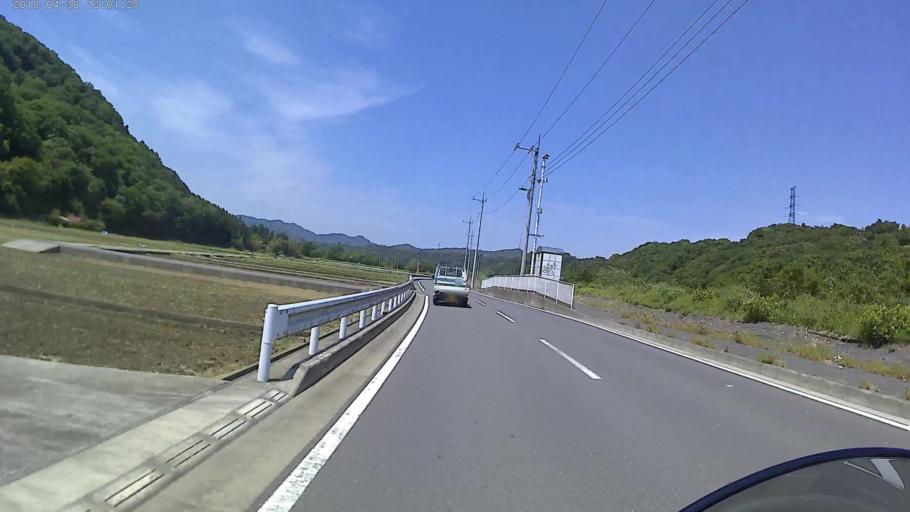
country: JP
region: Kanagawa
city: Zama
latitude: 35.5172
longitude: 139.3255
